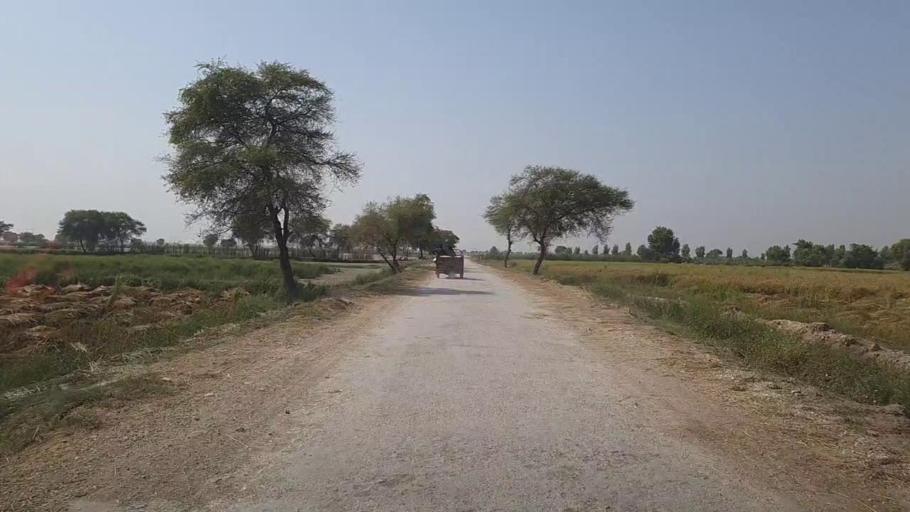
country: PK
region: Sindh
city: Kandhkot
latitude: 28.3936
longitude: 69.3162
